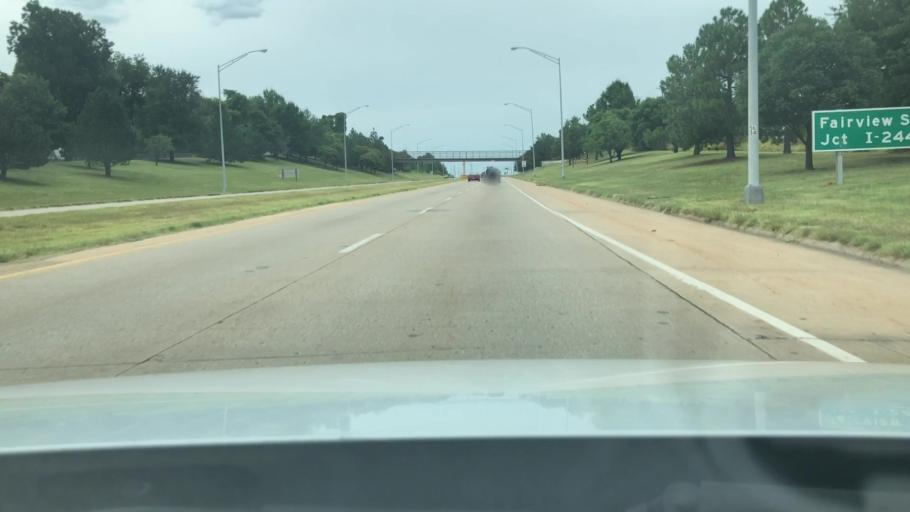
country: US
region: Oklahoma
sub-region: Tulsa County
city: Tulsa
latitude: 36.1716
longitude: -96.0008
